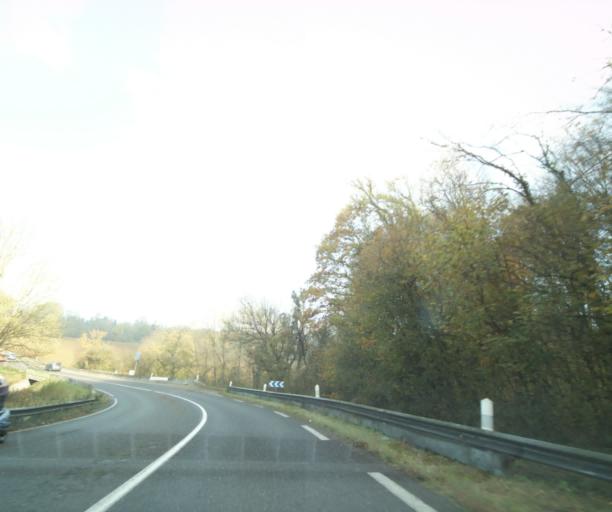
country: FR
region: Lorraine
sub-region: Departement de Meurthe-et-Moselle
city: Briey
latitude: 49.2679
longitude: 5.9273
